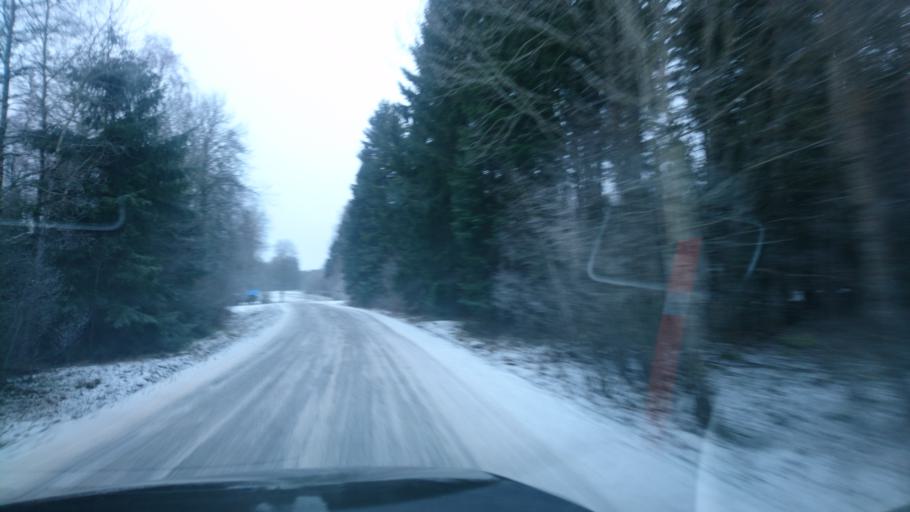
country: SE
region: Vaestra Goetaland
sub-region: Falkopings Kommun
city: Floby
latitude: 58.0766
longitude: 13.3889
